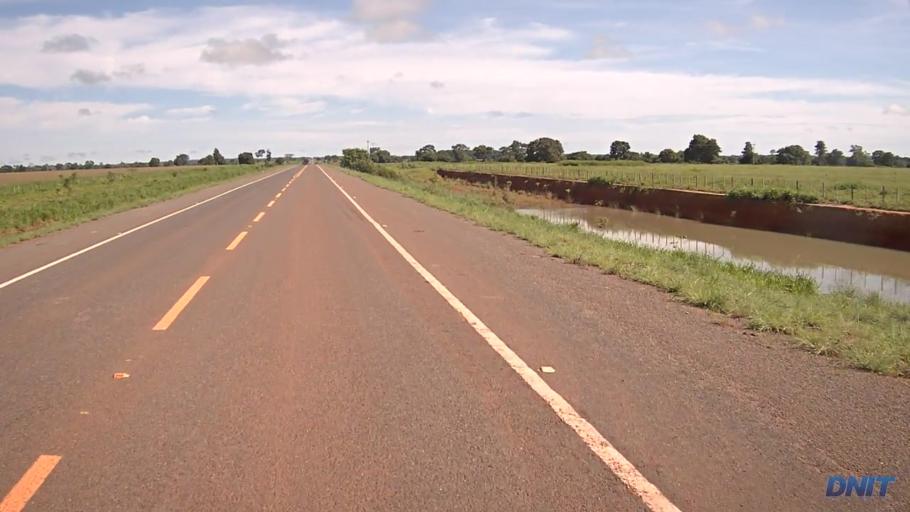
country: BR
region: Goias
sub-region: Sao Miguel Do Araguaia
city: Sao Miguel do Araguaia
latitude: -13.3927
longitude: -50.1374
